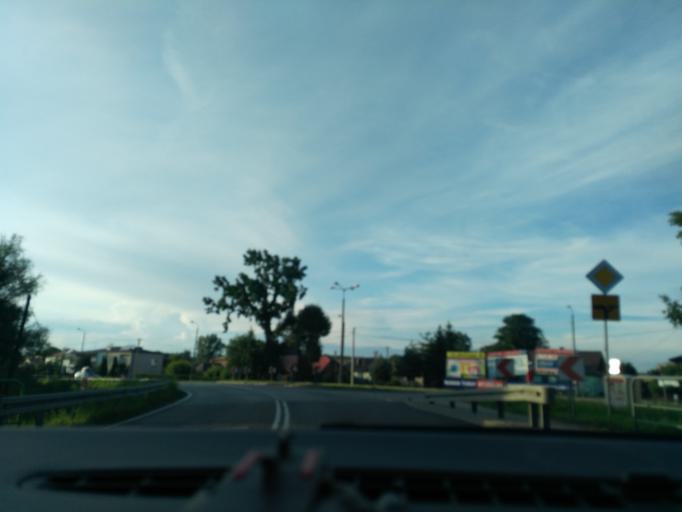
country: PL
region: Lublin Voivodeship
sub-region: Powiat krasnicki
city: Krasnik
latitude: 50.9032
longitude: 22.2727
